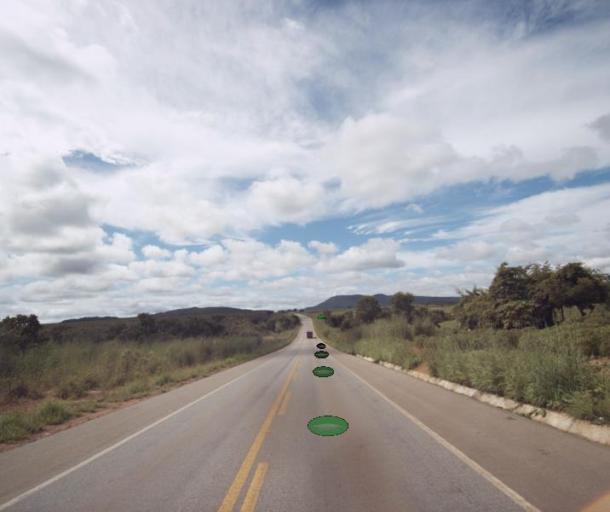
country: BR
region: Goias
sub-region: Barro Alto
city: Barro Alto
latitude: -15.1893
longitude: -48.7765
